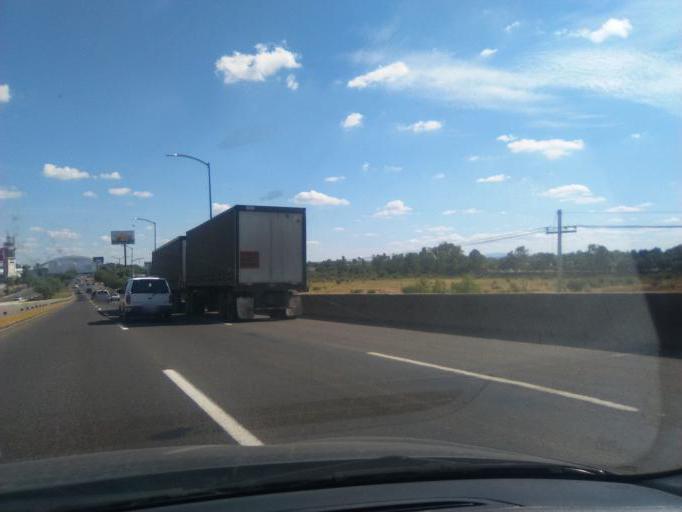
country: MX
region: Guanajuato
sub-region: Leon
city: Ladrilleras del Refugio
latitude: 21.0628
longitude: -101.5866
